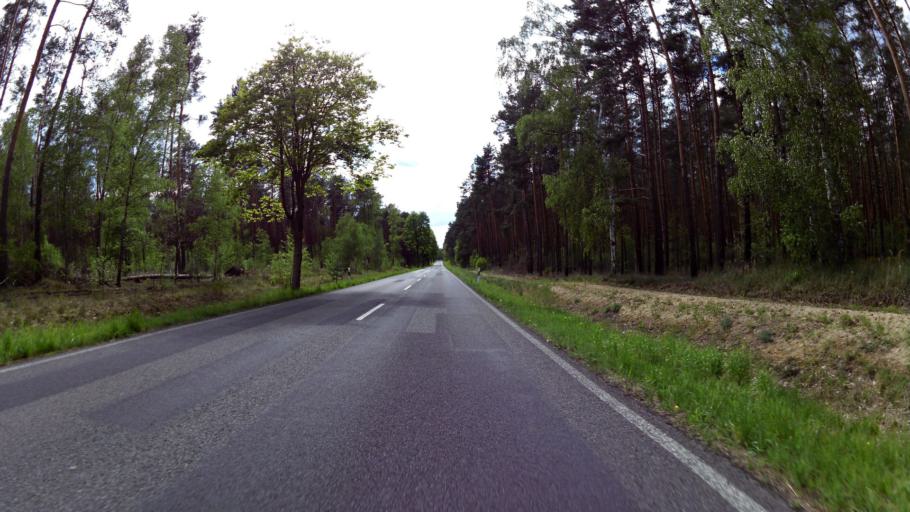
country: DE
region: Brandenburg
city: Rauen
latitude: 52.3412
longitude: 13.9791
